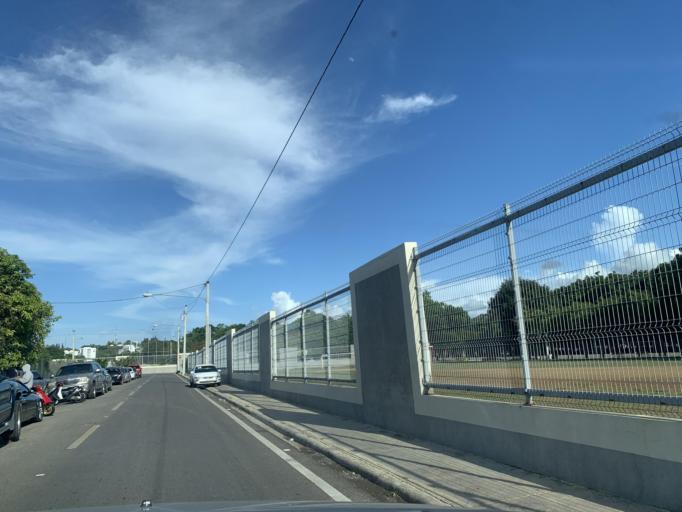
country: DO
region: Santiago
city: Santiago de los Caballeros
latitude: 19.4691
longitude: -70.6968
